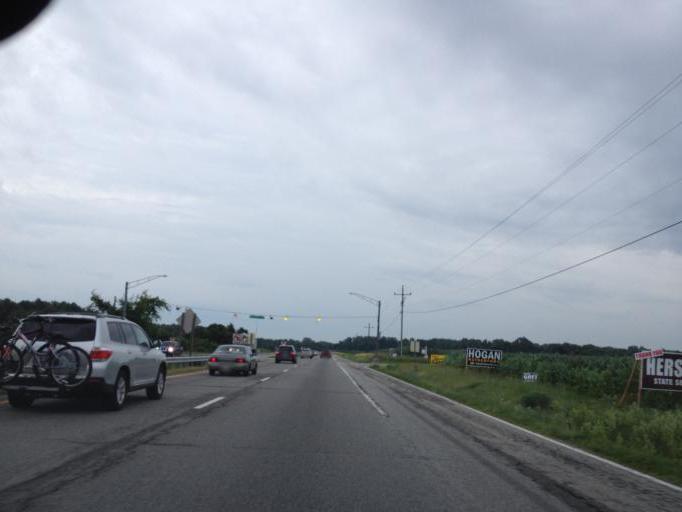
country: US
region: Maryland
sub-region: Queen Anne's County
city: Centreville
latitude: 38.9700
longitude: -76.1205
